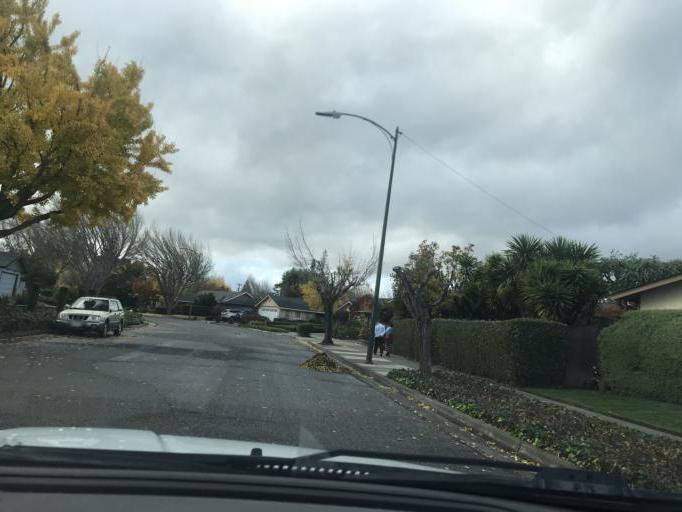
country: US
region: California
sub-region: Santa Clara County
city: Buena Vista
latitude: 37.3095
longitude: -121.9096
